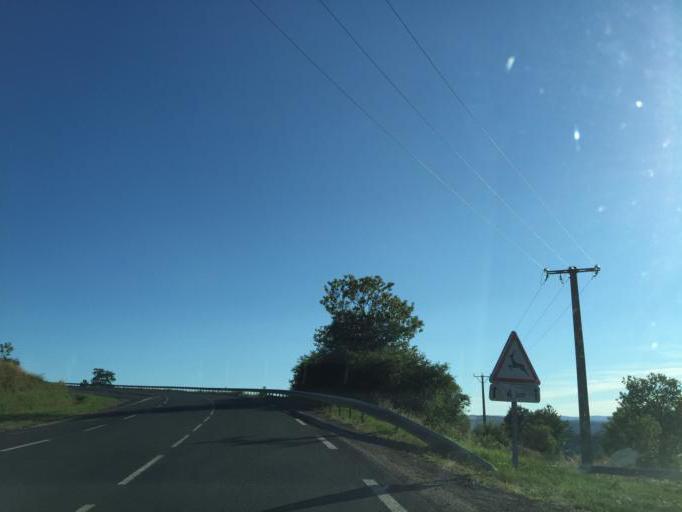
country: FR
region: Auvergne
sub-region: Departement de la Haute-Loire
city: Bains
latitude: 44.9977
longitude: 3.6908
